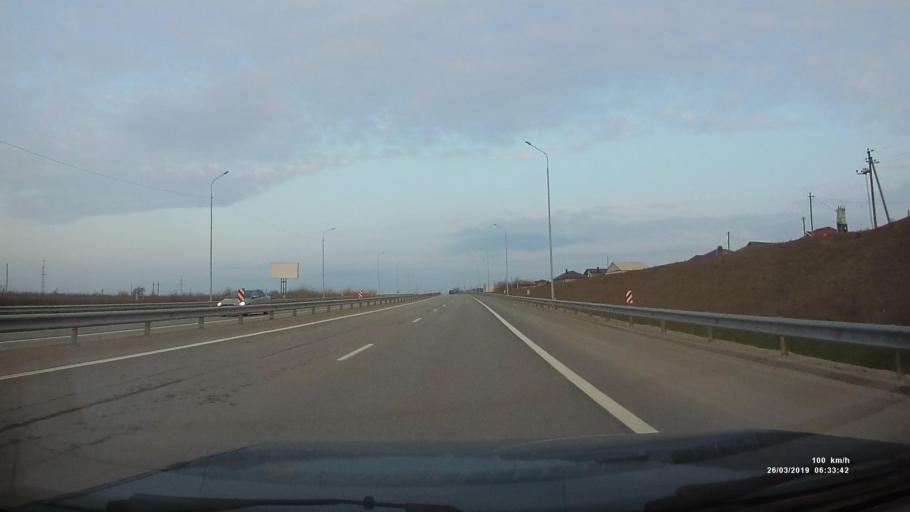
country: RU
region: Rostov
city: Chaltyr
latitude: 47.2745
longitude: 39.4828
